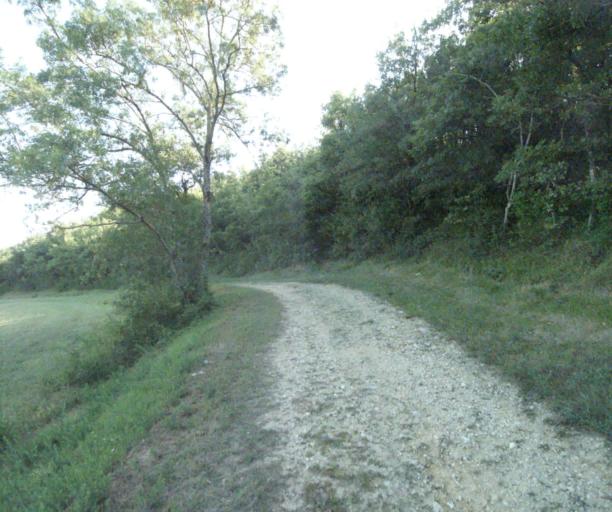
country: FR
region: Midi-Pyrenees
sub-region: Departement de la Haute-Garonne
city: Saint-Felix-Lauragais
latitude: 43.4384
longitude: 1.8201
